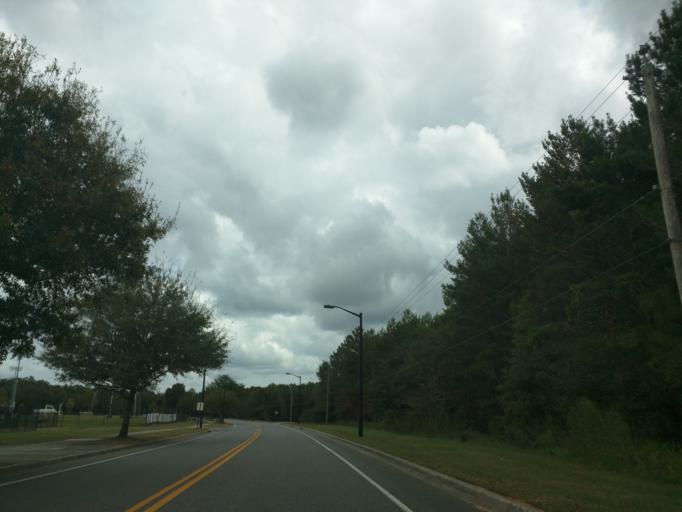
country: US
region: Florida
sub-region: Leon County
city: Woodville
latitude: 30.3823
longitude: -84.2230
